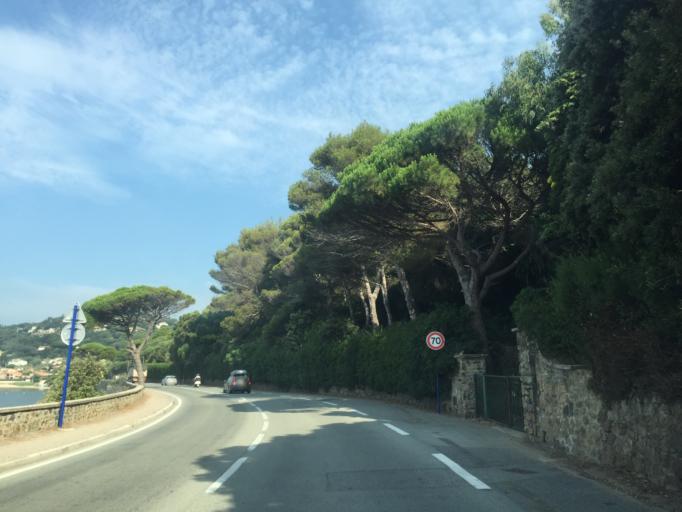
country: FR
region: Provence-Alpes-Cote d'Azur
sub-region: Departement du Var
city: Sainte-Maxime
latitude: 43.3130
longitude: 6.6672
